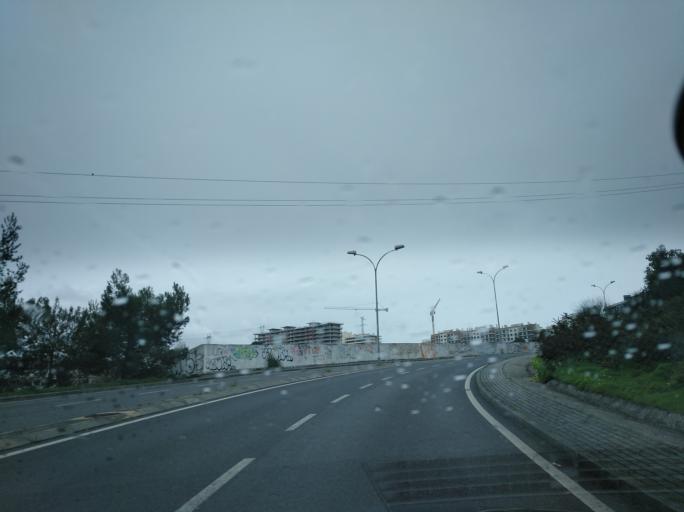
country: PT
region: Lisbon
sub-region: Odivelas
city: Odivelas
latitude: 38.7852
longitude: -9.1955
